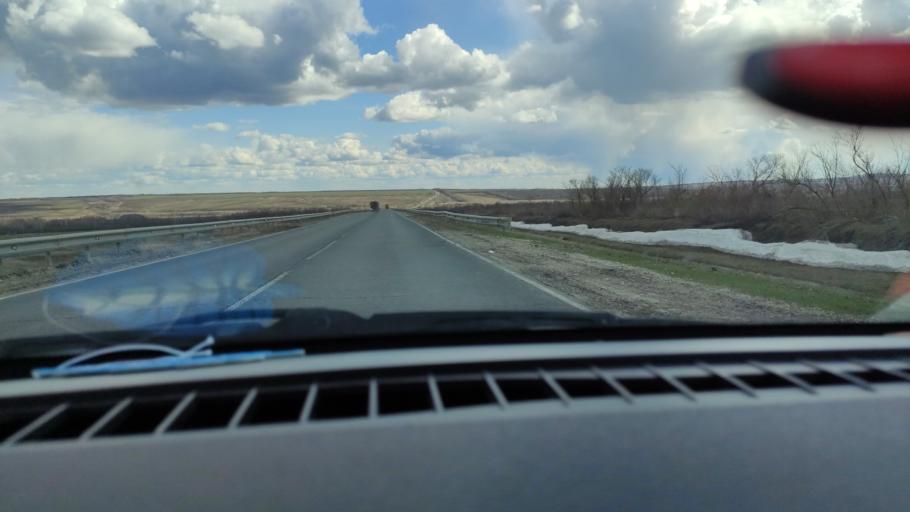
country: RU
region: Saratov
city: Dukhovnitskoye
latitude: 52.7537
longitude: 48.2463
